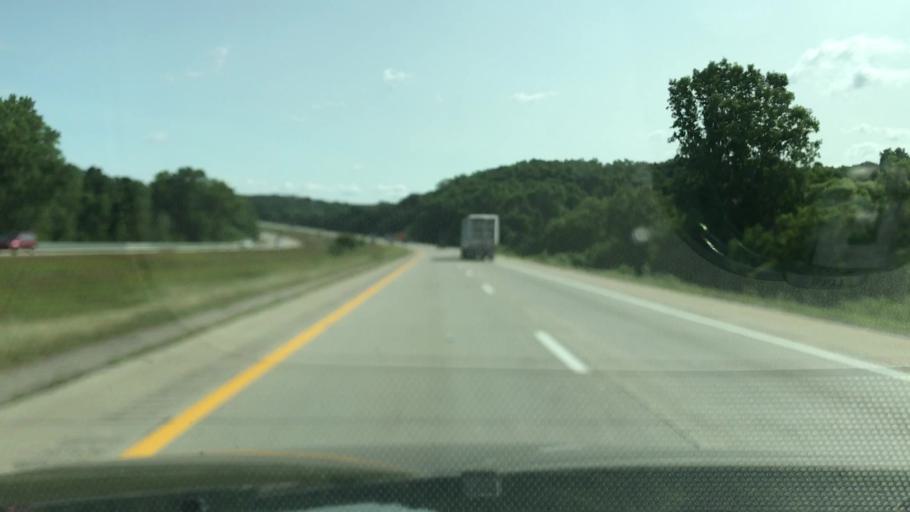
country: US
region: Michigan
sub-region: Kent County
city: Comstock Park
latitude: 43.0723
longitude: -85.6469
